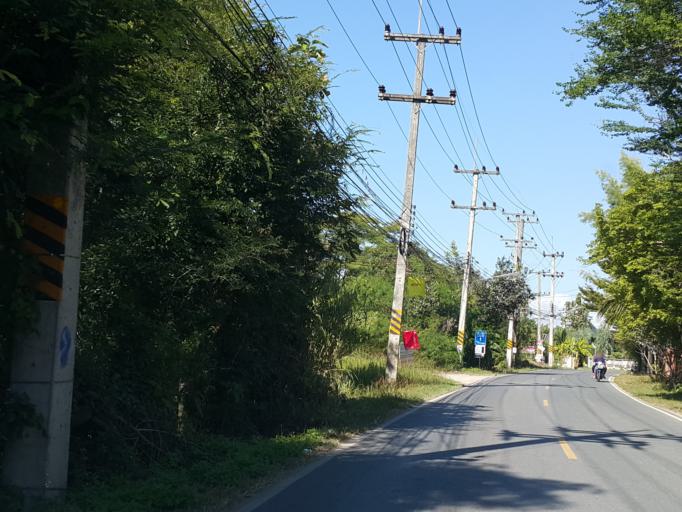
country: TH
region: Chiang Mai
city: San Sai
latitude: 18.9514
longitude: 98.9248
